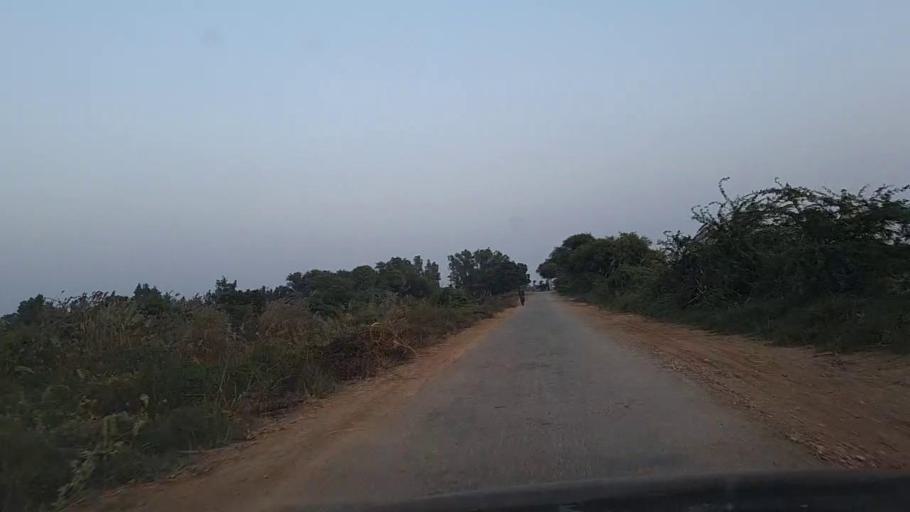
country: PK
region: Sindh
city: Mirpur Sakro
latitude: 24.6280
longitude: 67.6495
